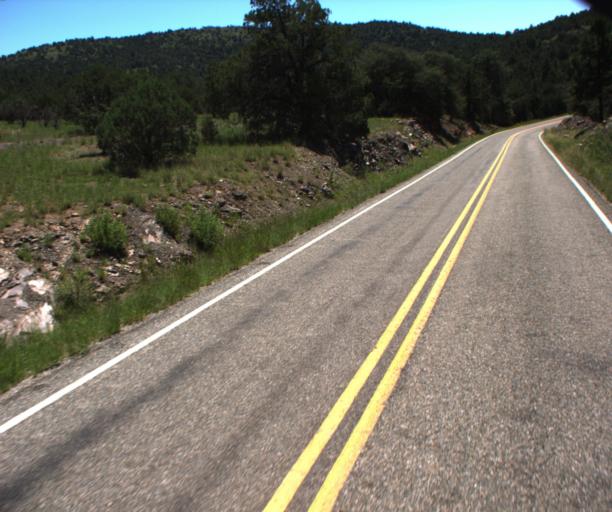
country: US
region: Arizona
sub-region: Greenlee County
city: Morenci
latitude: 33.2846
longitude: -109.3550
